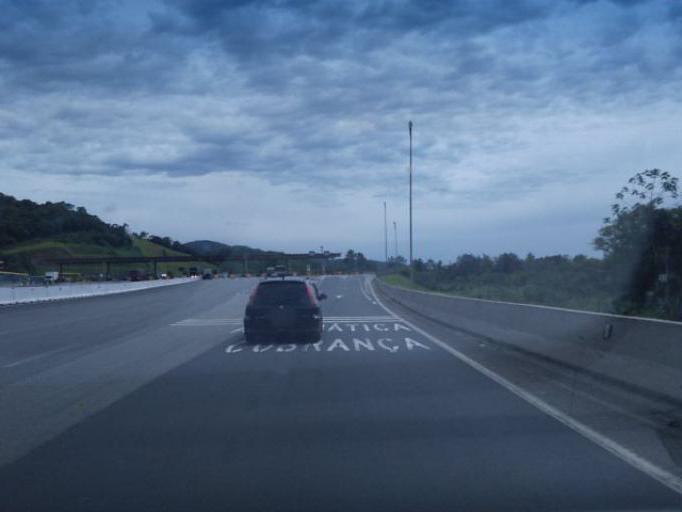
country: BR
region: Sao Paulo
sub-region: Miracatu
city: Miracatu
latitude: -24.1563
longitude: -47.3256
